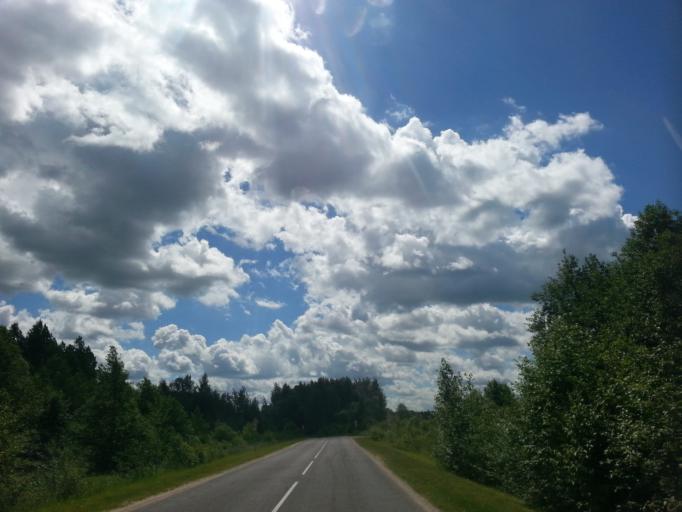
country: BY
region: Vitebsk
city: Mosar
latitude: 55.1410
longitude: 27.3220
